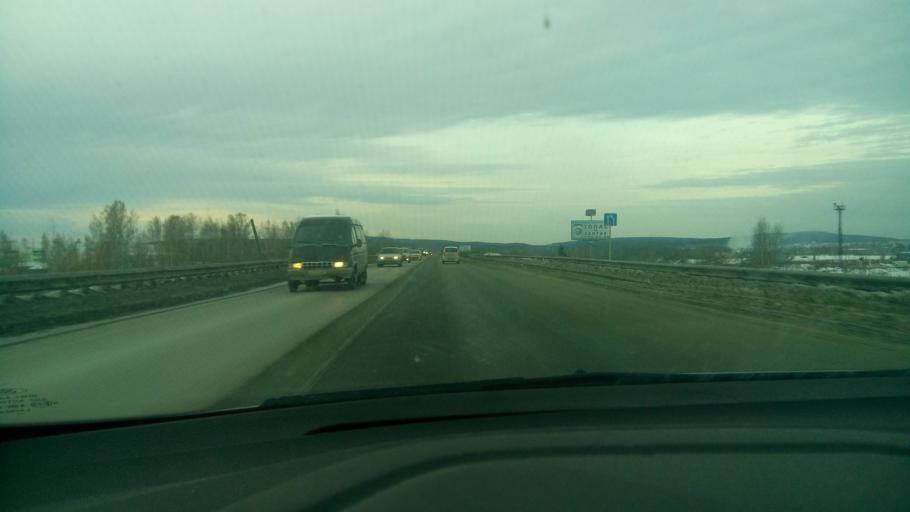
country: RU
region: Sverdlovsk
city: Istok
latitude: 56.7539
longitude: 60.7579
